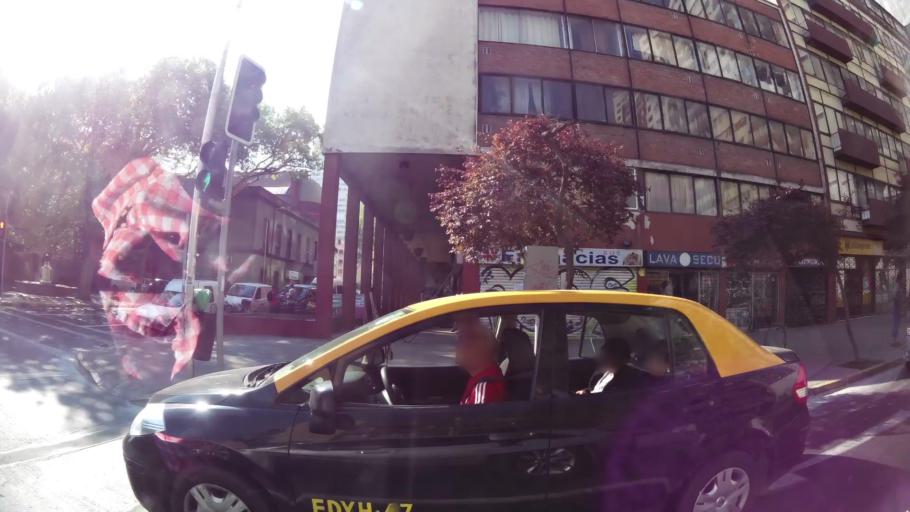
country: CL
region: Santiago Metropolitan
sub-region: Provincia de Santiago
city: Santiago
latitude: -33.4381
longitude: -70.6581
